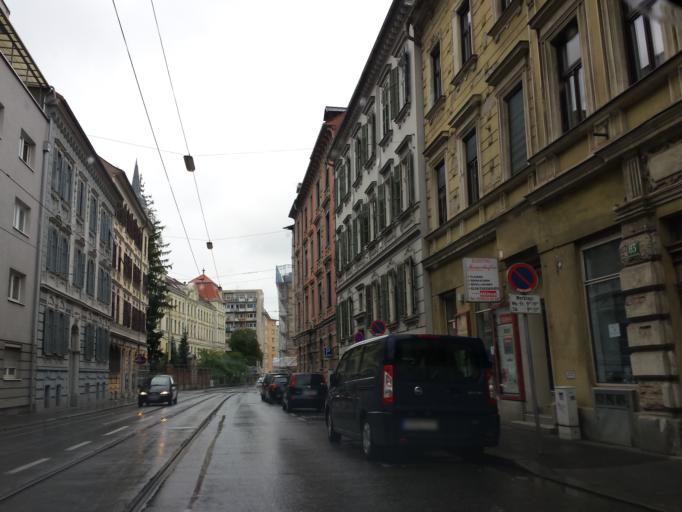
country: AT
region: Styria
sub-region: Graz Stadt
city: Graz
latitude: 47.0750
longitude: 15.4578
